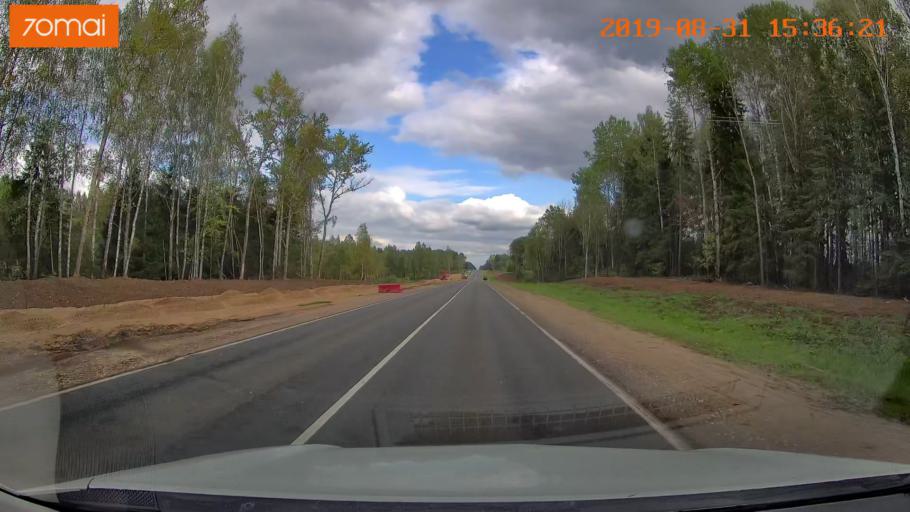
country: RU
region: Kaluga
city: Mosal'sk
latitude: 54.6107
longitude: 34.7570
